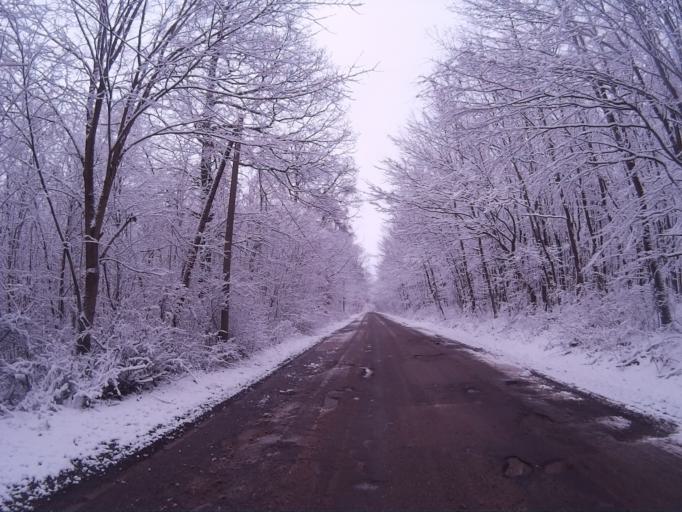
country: HU
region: Komarom-Esztergom
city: Tarjan
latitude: 47.5788
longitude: 18.4908
